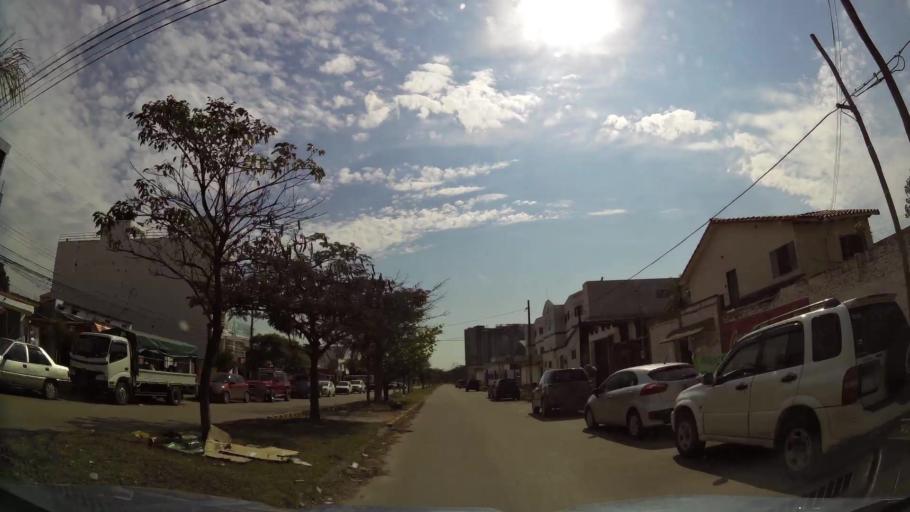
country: BO
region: Santa Cruz
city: Santa Cruz de la Sierra
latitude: -17.7306
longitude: -63.1691
